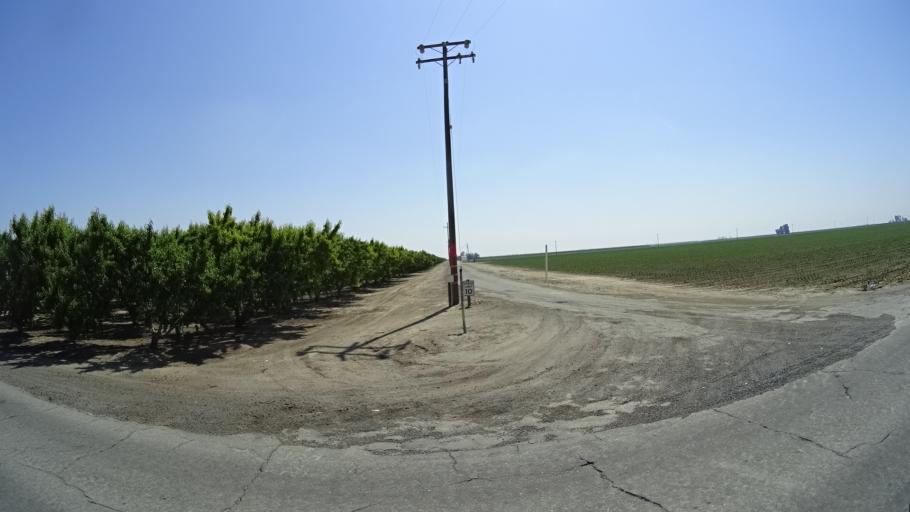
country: US
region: California
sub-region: Fresno County
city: Kingsburg
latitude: 36.4234
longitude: -119.5287
